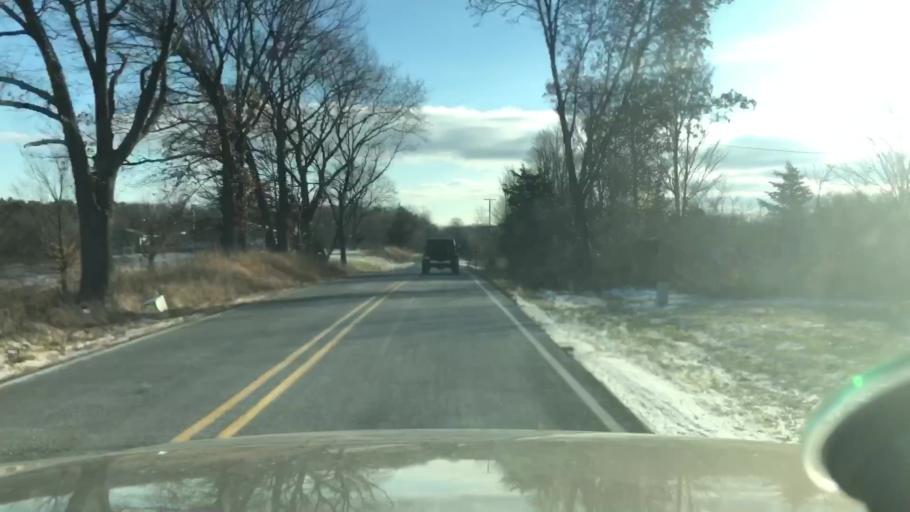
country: US
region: Michigan
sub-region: Jackson County
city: Vandercook Lake
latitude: 42.1195
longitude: -84.4514
